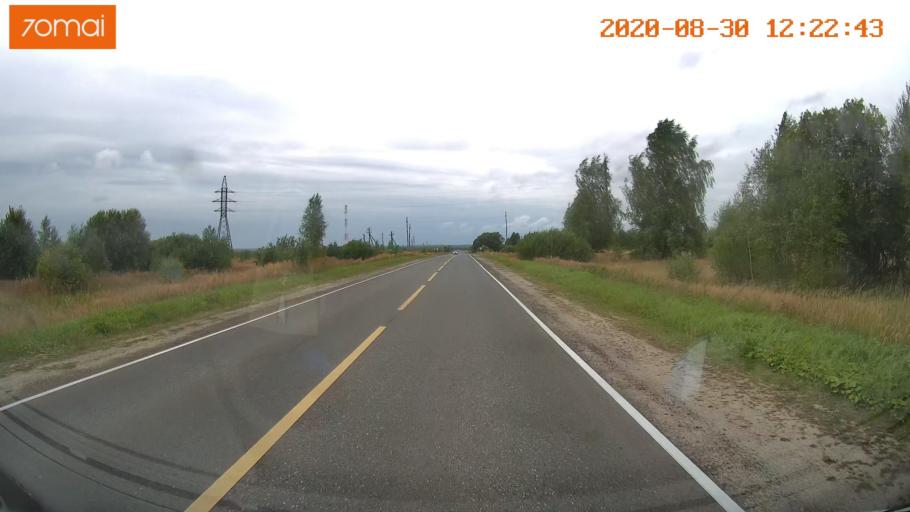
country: RU
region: Ivanovo
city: Yur'yevets
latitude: 57.3307
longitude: 42.8425
